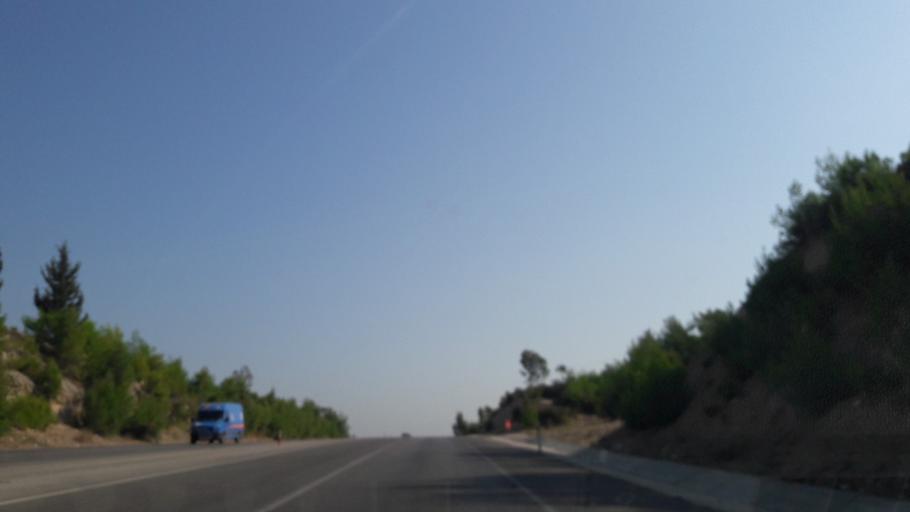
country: TR
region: Adana
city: Sagkaya
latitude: 37.1539
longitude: 35.5467
